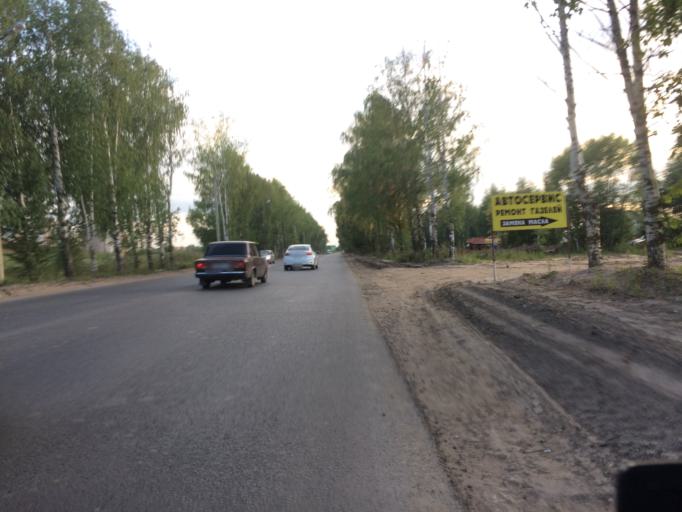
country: RU
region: Mariy-El
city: Medvedevo
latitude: 56.6525
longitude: 47.8375
